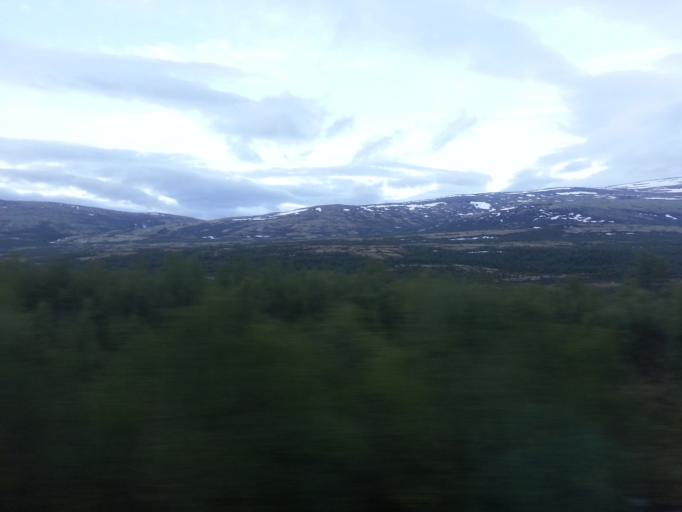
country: NO
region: Oppland
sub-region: Dovre
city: Dovre
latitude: 62.1981
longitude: 9.5112
